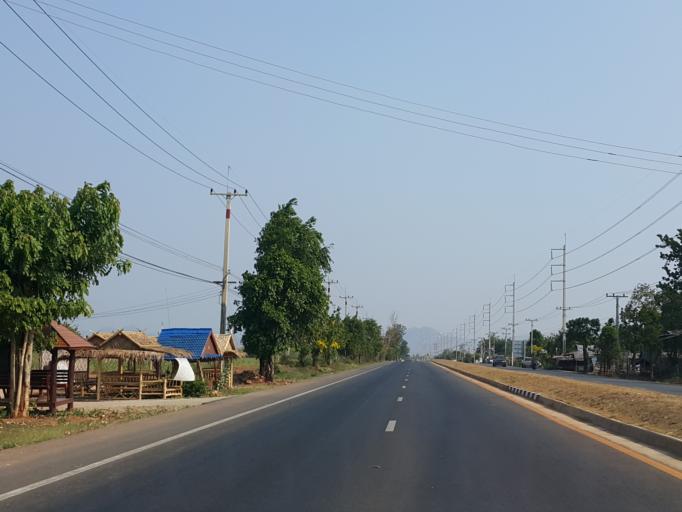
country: TH
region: Kanchanaburi
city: Kanchanaburi
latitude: 14.0744
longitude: 99.3886
